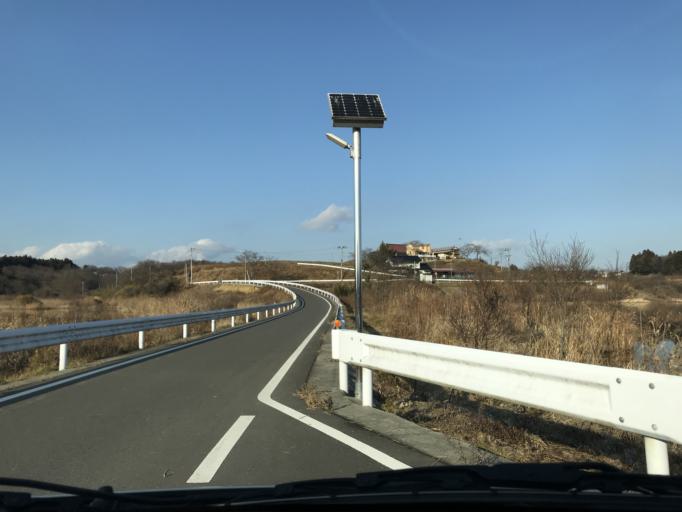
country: JP
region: Miyagi
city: Wakuya
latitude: 38.6890
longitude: 141.1066
